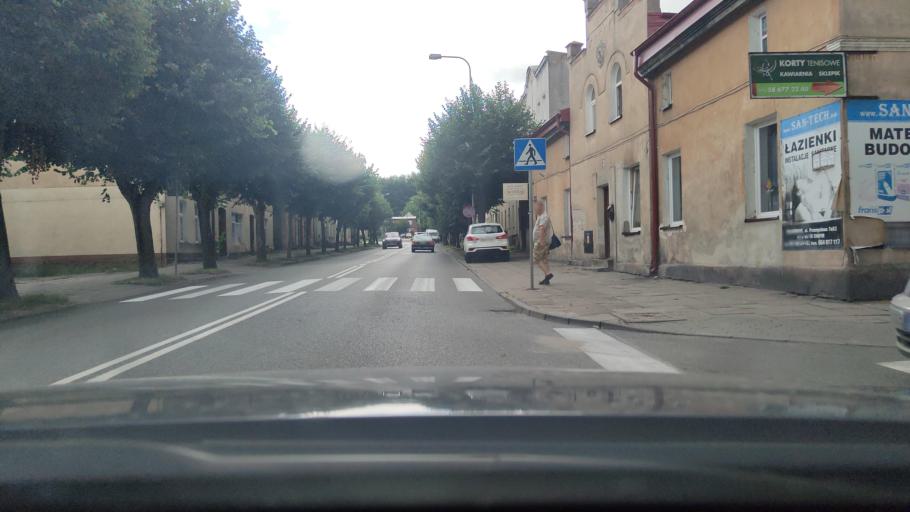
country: PL
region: Pomeranian Voivodeship
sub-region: Powiat wejherowski
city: Wejherowo
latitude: 54.5992
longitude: 18.2325
